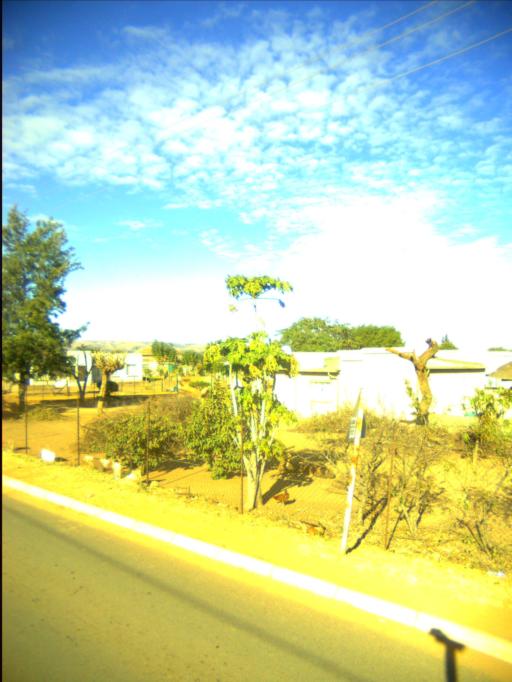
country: ZA
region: Mpumalanga
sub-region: Nkangala District Municipality
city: Siyabuswa
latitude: -25.1507
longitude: 28.9678
